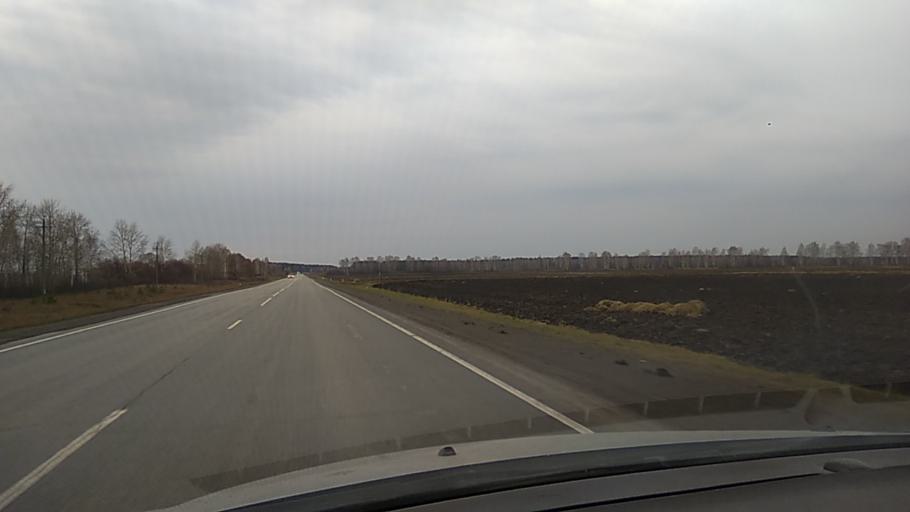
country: RU
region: Sverdlovsk
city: Talitsa
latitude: 57.0526
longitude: 63.5069
